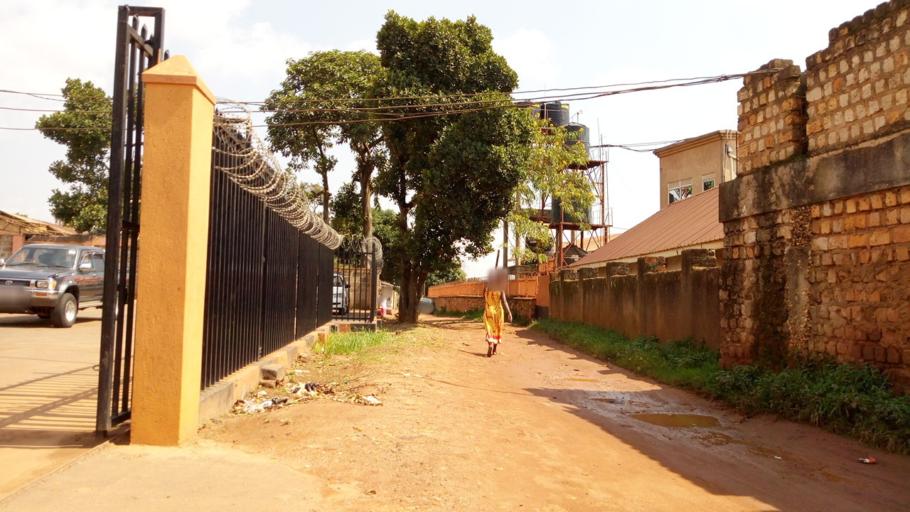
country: UG
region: Central Region
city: Kampala Central Division
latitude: 0.3459
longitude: 32.5661
